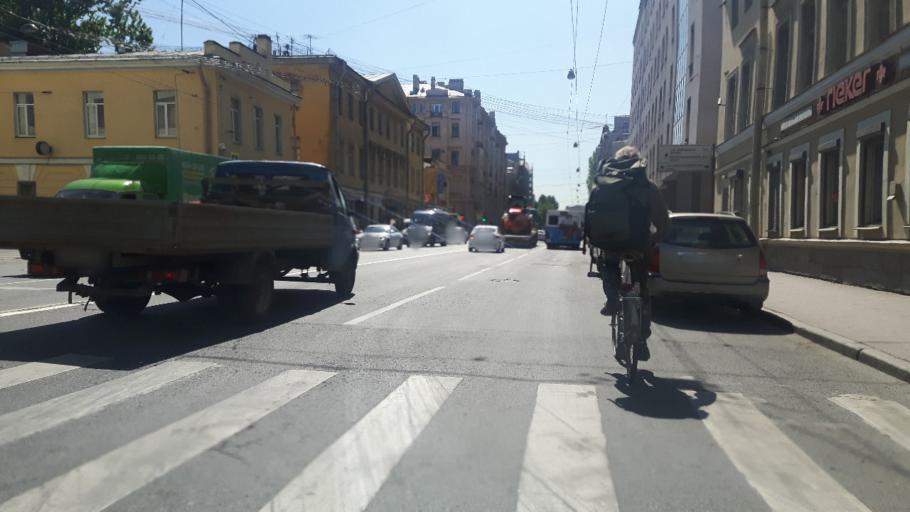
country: RU
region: St.-Petersburg
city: Admiralteisky
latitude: 59.9139
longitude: 30.2973
